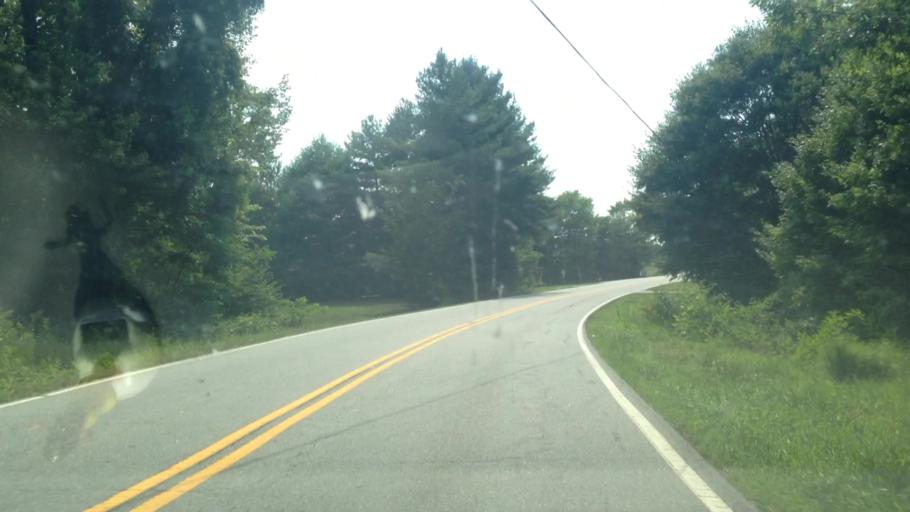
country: US
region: North Carolina
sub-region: Forsyth County
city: Walkertown
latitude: 36.2264
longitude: -80.1161
